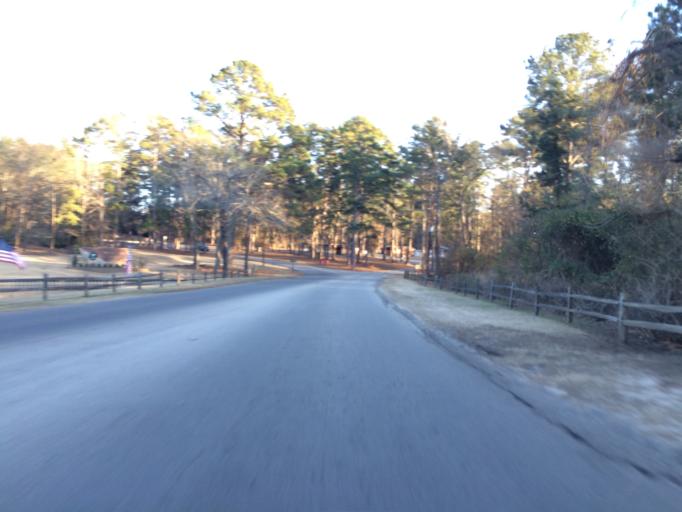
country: US
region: Texas
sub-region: Wood County
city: Hawkins
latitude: 32.7149
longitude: -95.1975
